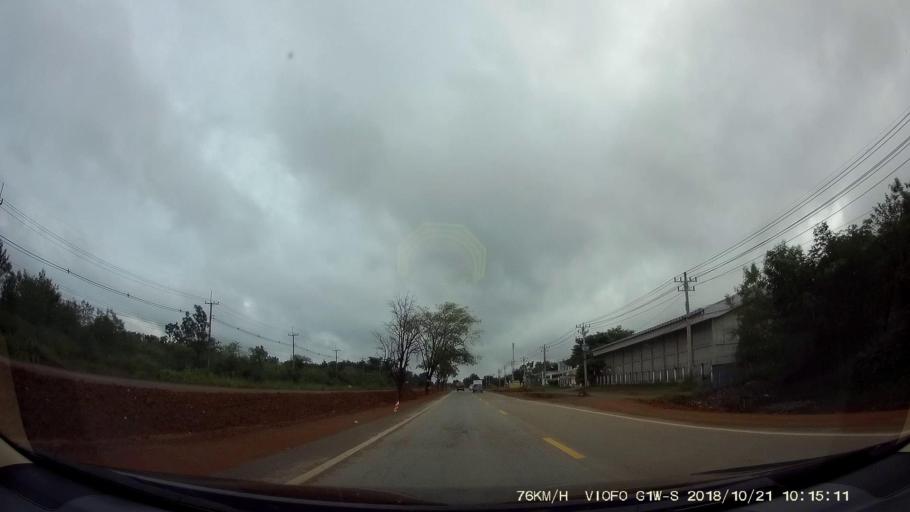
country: TH
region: Chaiyaphum
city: Phu Khiao
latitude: 16.3431
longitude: 102.1631
